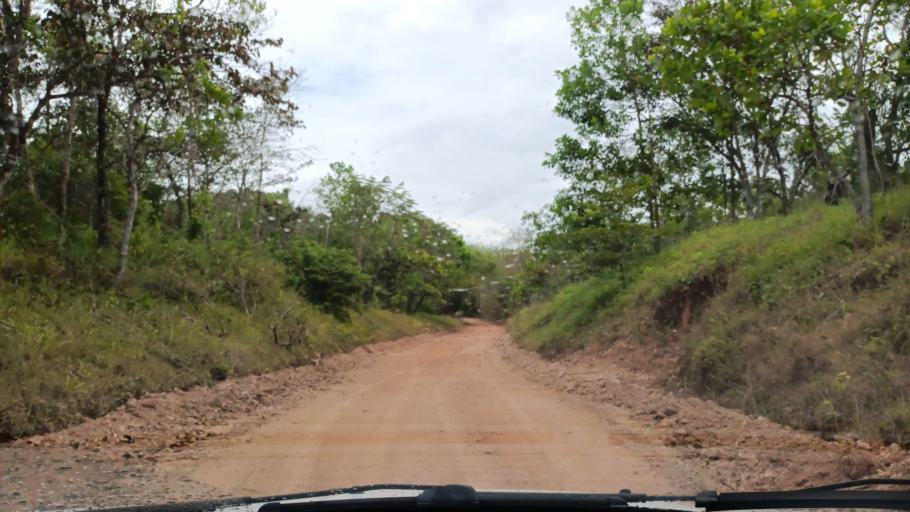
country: PA
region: Panama
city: La Cabima
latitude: 9.1280
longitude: -79.5061
